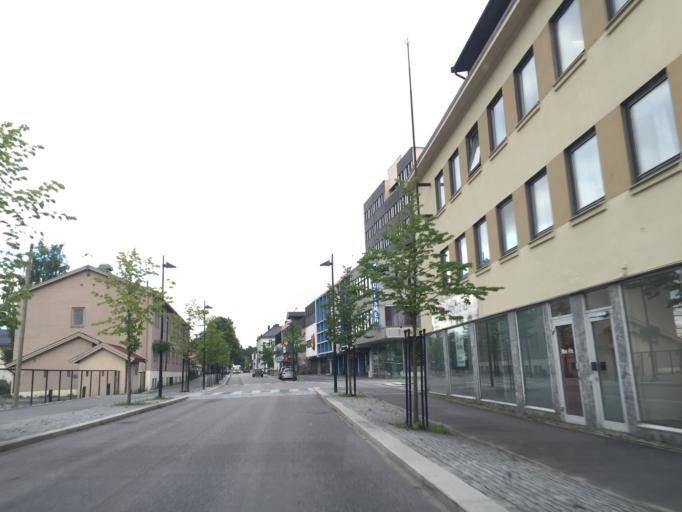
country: NO
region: Hedmark
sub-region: Kongsvinger
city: Kongsvinger
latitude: 60.1875
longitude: 12.0008
